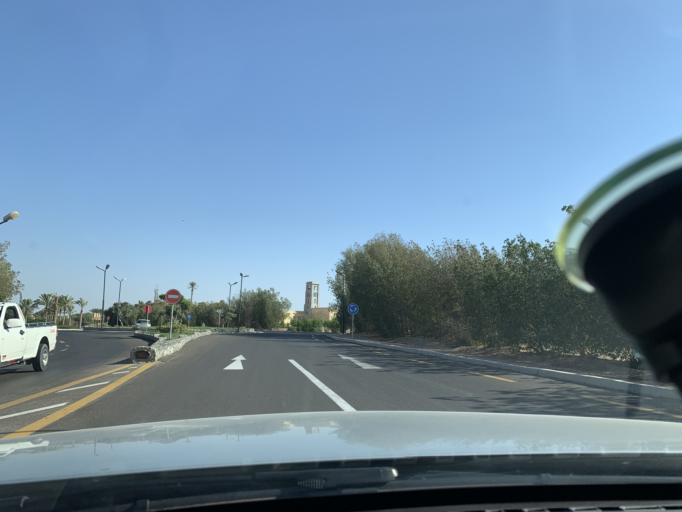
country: EG
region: Red Sea
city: El Gouna
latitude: 27.4014
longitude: 33.6699
